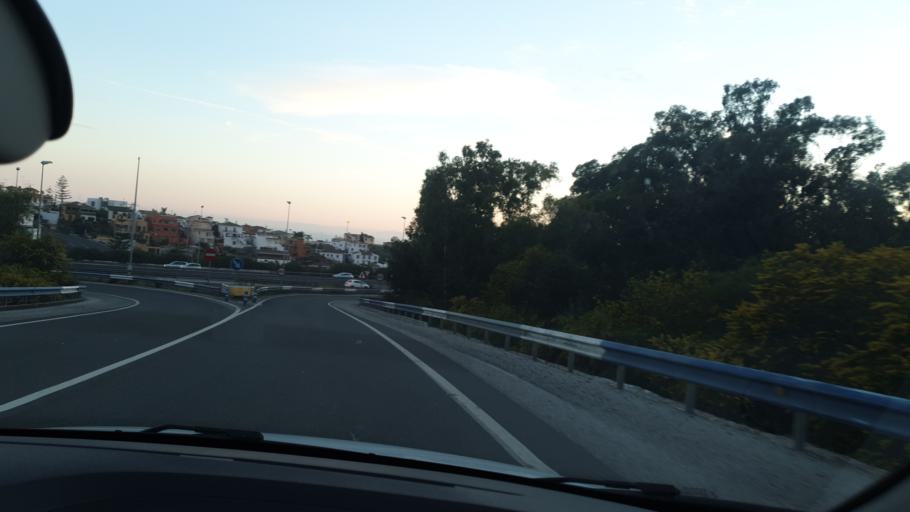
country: ES
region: Andalusia
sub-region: Provincia de Malaga
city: Marbella
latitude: 36.5218
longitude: -4.8819
